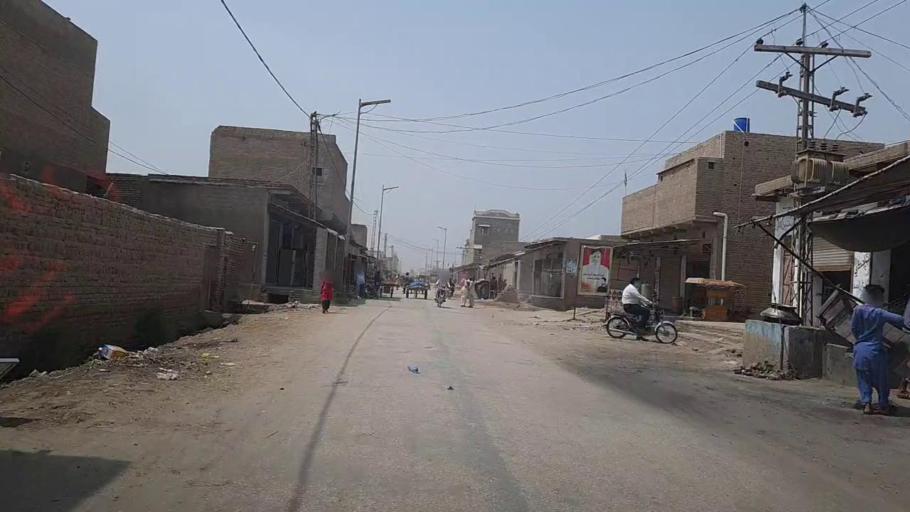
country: PK
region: Sindh
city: Radhan
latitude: 27.1732
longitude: 67.9477
